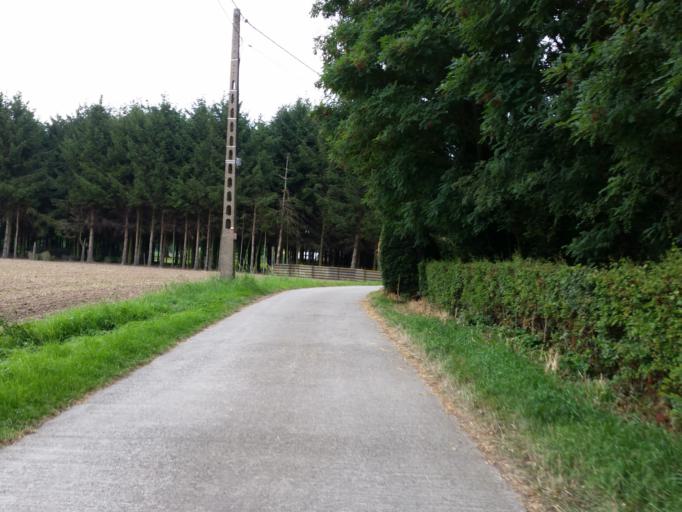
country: BE
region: Flanders
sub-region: Provincie Vlaams-Brabant
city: Zemst
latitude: 50.9771
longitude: 4.4405
